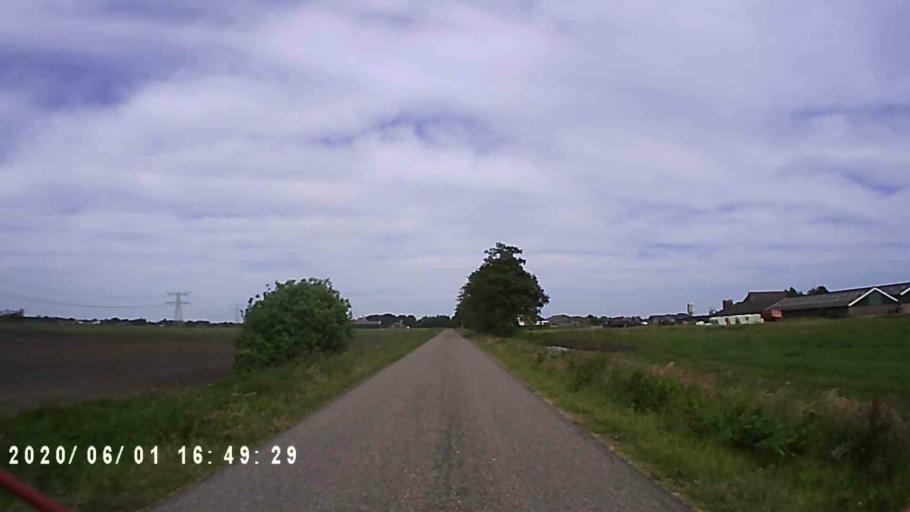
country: NL
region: Friesland
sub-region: Gemeente Tytsjerksteradiel
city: Tytsjerk
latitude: 53.1873
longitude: 5.9065
